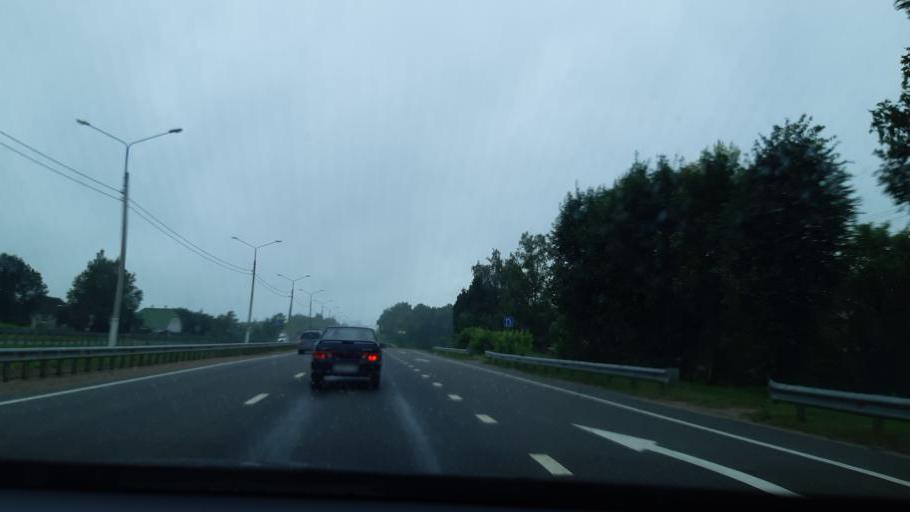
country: RU
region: Smolensk
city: Talashkino
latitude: 54.6741
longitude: 32.1468
